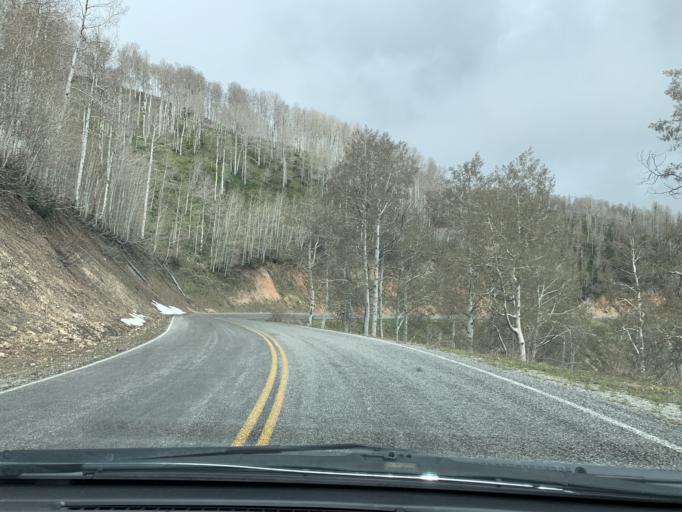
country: US
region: Utah
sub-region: Utah County
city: Elk Ridge
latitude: 39.8700
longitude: -111.6855
